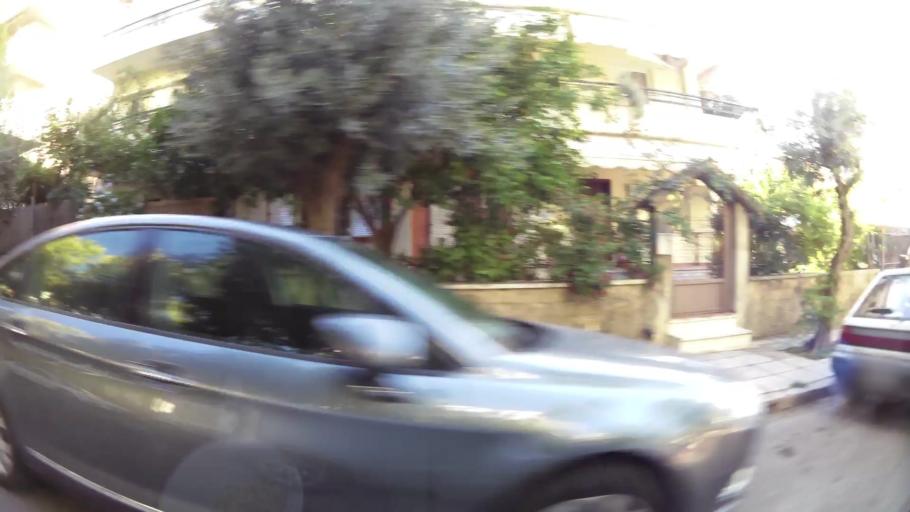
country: GR
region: Attica
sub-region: Nomarchia Athinas
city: Marousi
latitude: 38.0530
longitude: 23.7963
